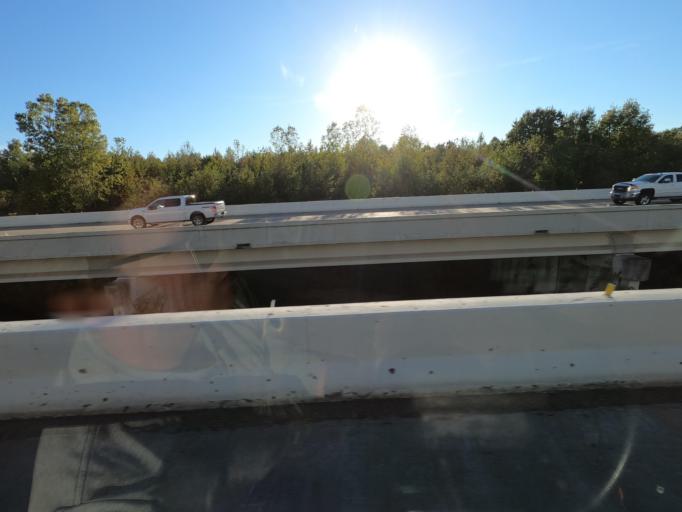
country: US
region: Tennessee
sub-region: Shelby County
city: Arlington
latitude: 35.2938
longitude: -89.6910
